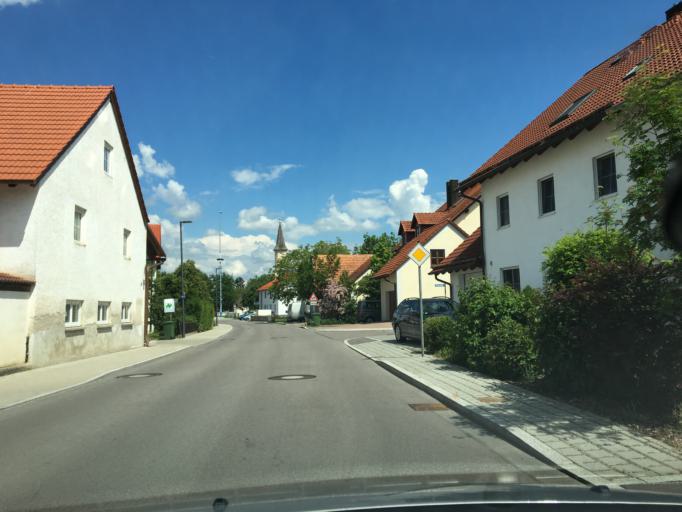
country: DE
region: Bavaria
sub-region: Upper Bavaria
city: Fahrenzhausen
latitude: 48.3441
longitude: 11.5738
